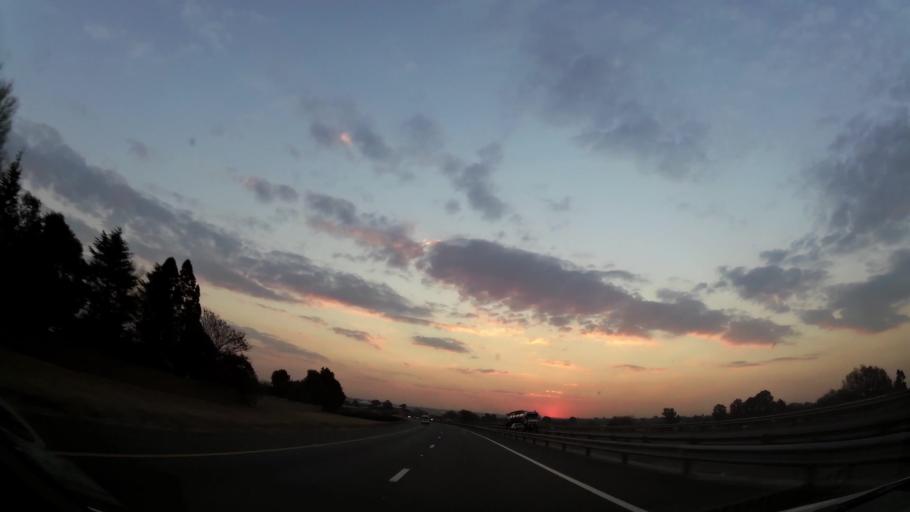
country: ZA
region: Gauteng
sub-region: Ekurhuleni Metropolitan Municipality
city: Brakpan
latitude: -26.2598
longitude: 28.3413
